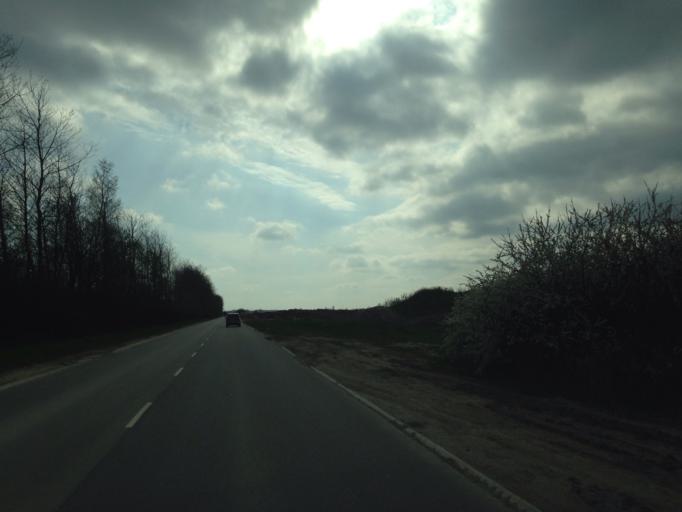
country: DK
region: Zealand
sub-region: Greve Kommune
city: Greve
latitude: 55.6113
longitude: 12.3050
